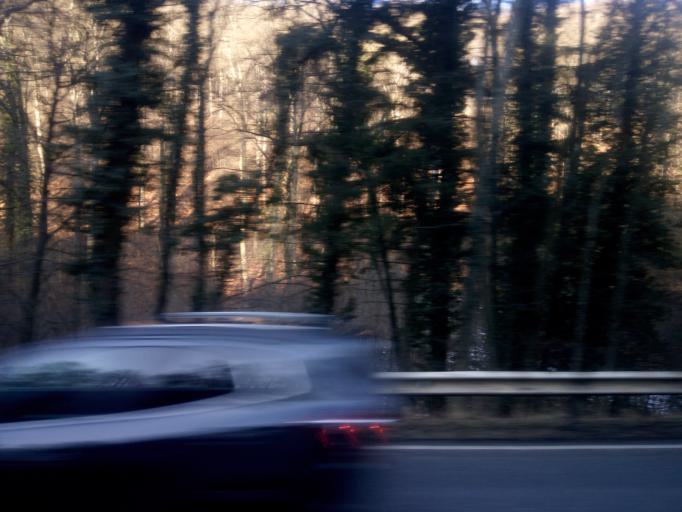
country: LU
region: Luxembourg
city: Kirchberg
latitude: 49.6432
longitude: 6.1640
